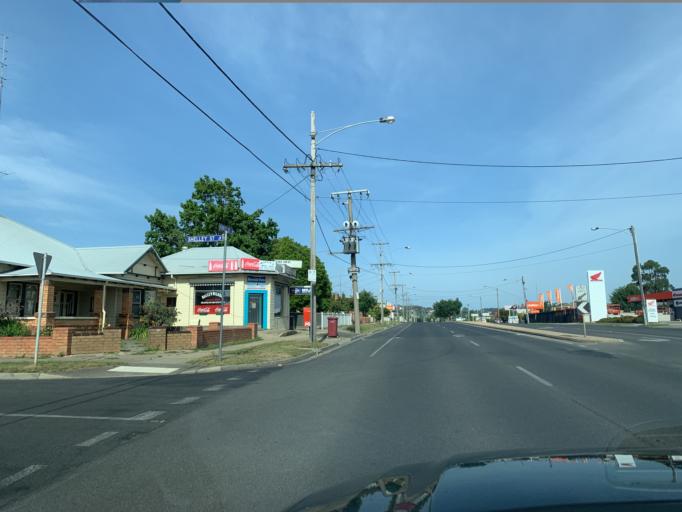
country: AU
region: Victoria
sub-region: Ballarat North
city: Lake Wendouree
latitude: -37.5417
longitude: 143.8439
